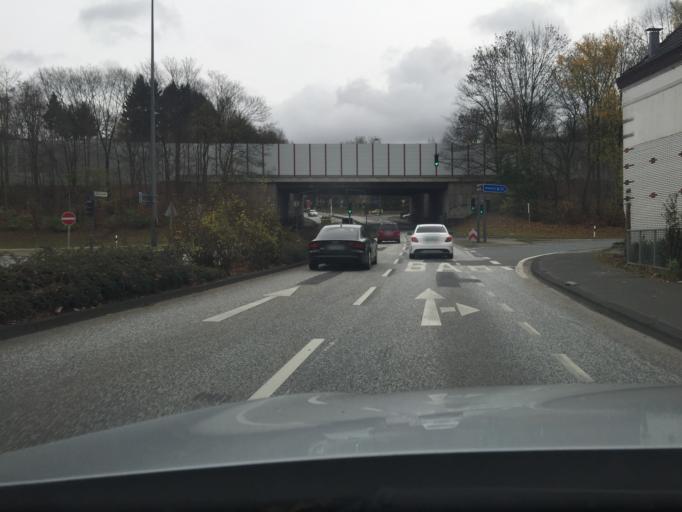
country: DE
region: North Rhine-Westphalia
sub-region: Regierungsbezirk Dusseldorf
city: Wuppertal
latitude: 51.2531
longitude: 7.1057
